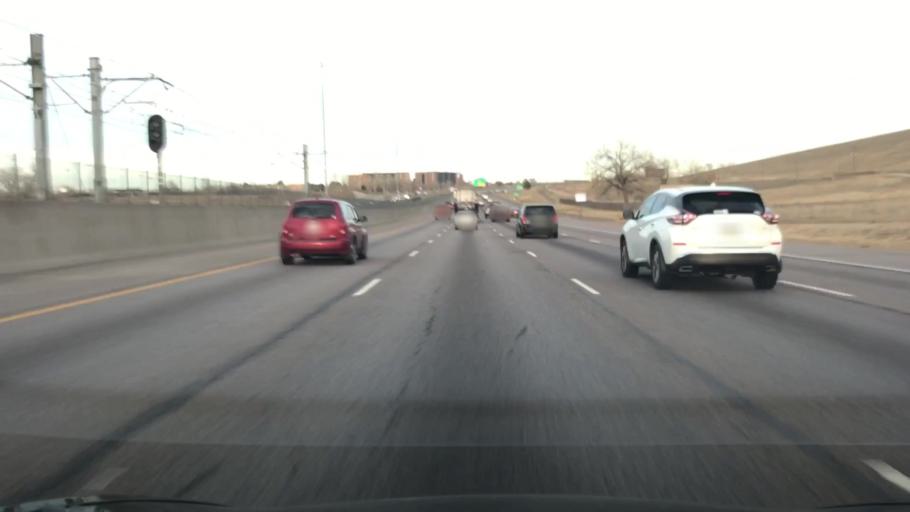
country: US
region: Colorado
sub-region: Arapahoe County
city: Centennial
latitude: 39.6514
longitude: -104.8595
